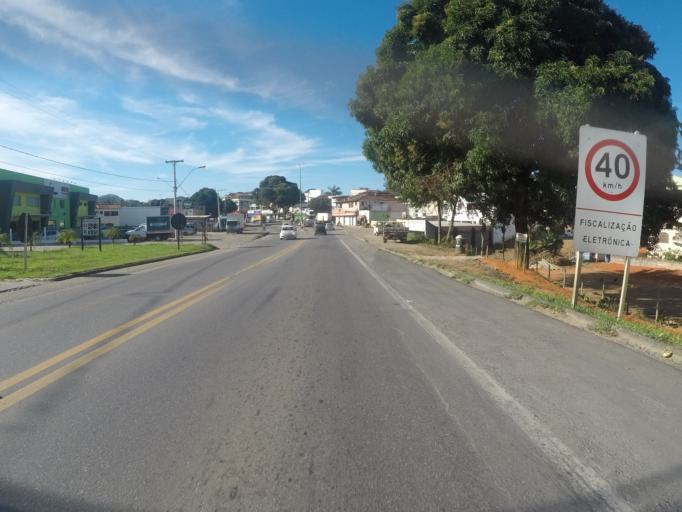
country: BR
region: Espirito Santo
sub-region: Fundao
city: Fundao
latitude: -19.9350
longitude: -40.4056
